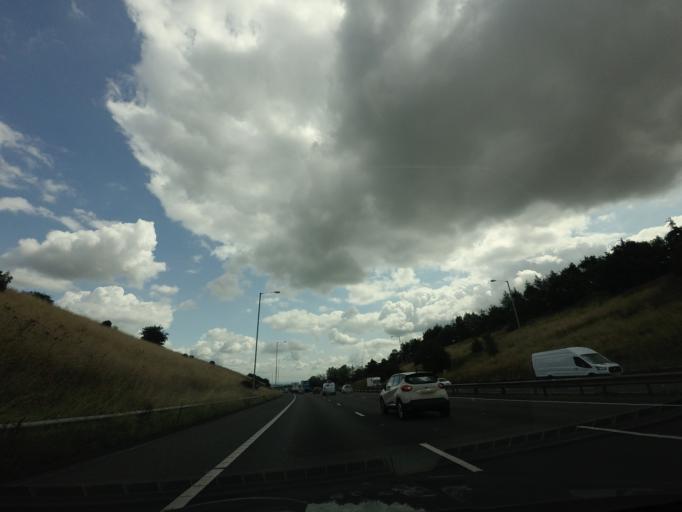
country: GB
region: England
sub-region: St. Helens
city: Billinge
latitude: 53.5128
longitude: -2.6860
